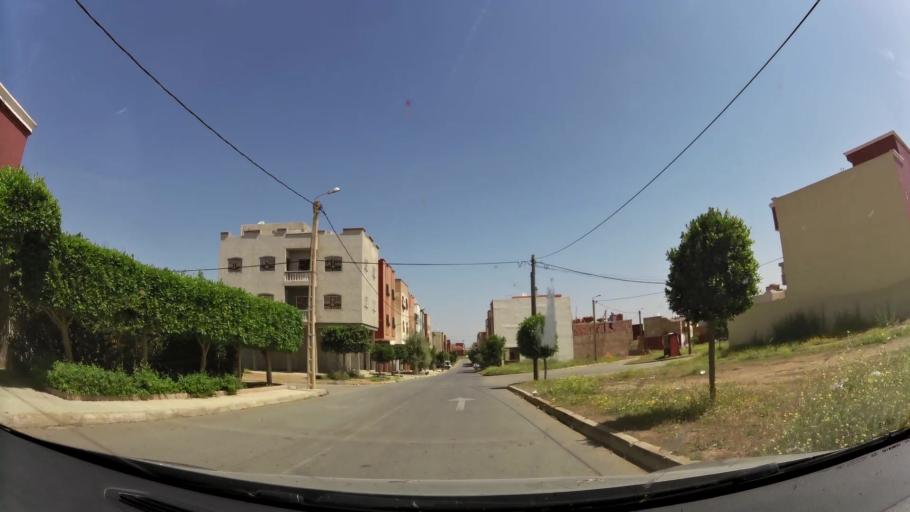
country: MA
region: Rabat-Sale-Zemmour-Zaer
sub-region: Khemisset
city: Khemisset
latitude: 33.8060
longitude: -6.0887
